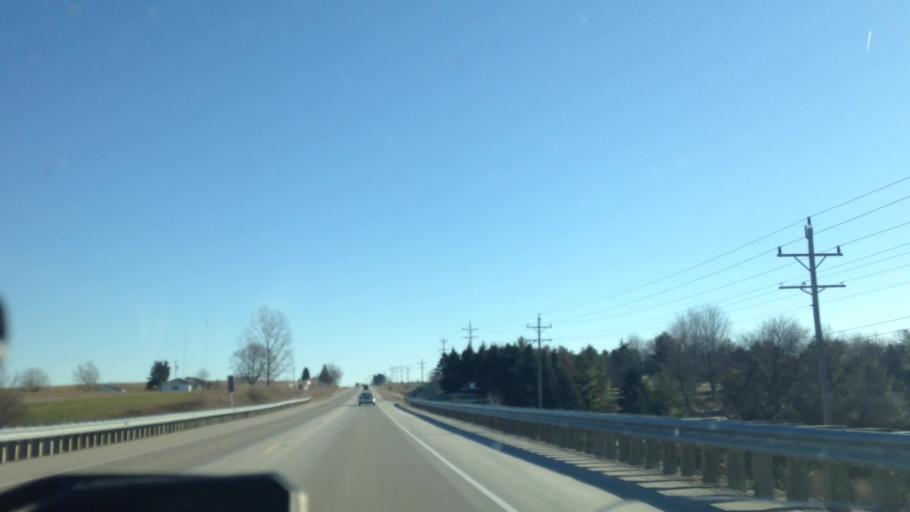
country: US
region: Wisconsin
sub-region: Washington County
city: Slinger
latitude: 43.4275
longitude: -88.3198
